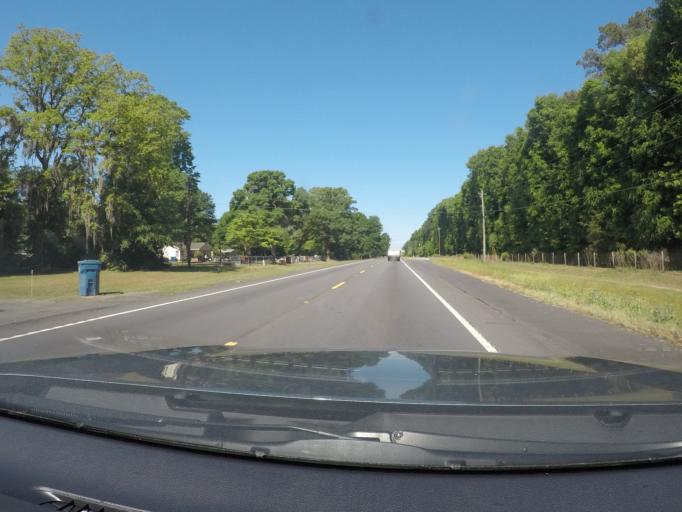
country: US
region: Georgia
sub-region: Chatham County
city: Bloomingdale
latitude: 32.1933
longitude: -81.4255
